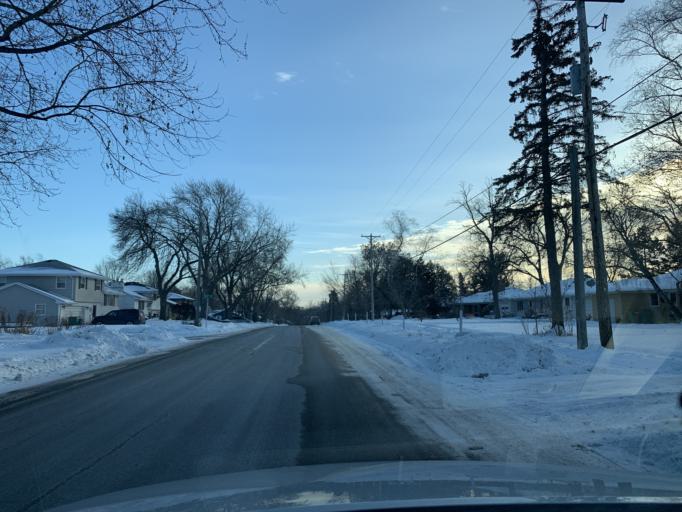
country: US
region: Minnesota
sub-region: Hennepin County
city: Minnetonka Mills
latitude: 44.9589
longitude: -93.3962
